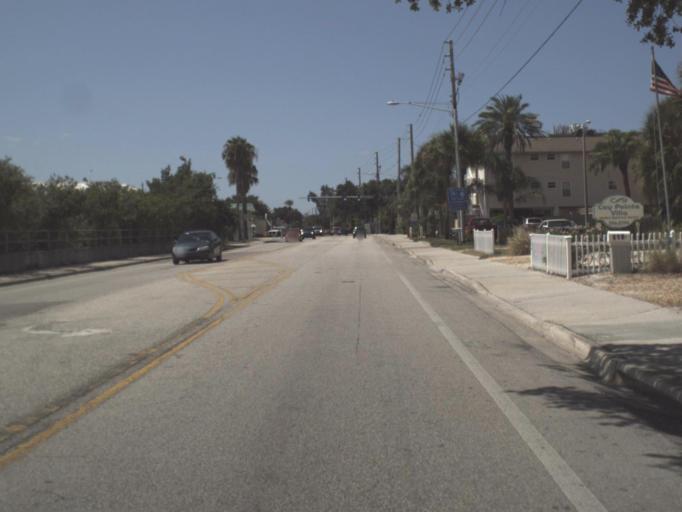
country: US
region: Florida
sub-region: Pinellas County
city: Indian Rocks Beach
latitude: 27.8855
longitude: -82.8505
